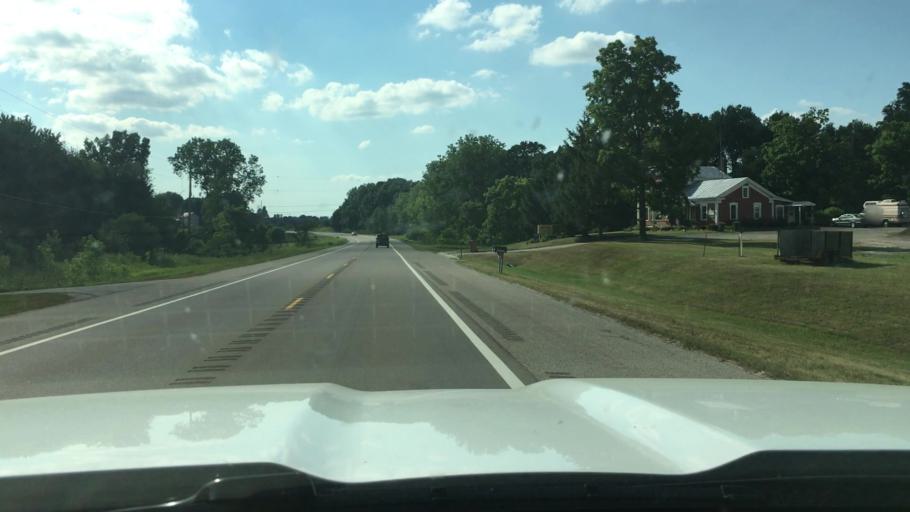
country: US
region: Michigan
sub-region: Kent County
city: Forest Hills
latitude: 43.0847
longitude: -85.4195
